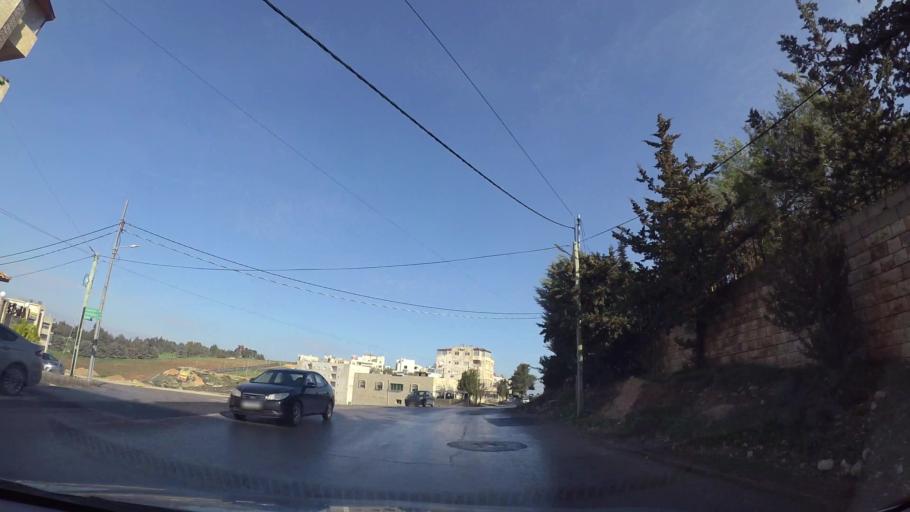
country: JO
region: Amman
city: Al Jubayhah
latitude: 32.0080
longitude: 35.8502
